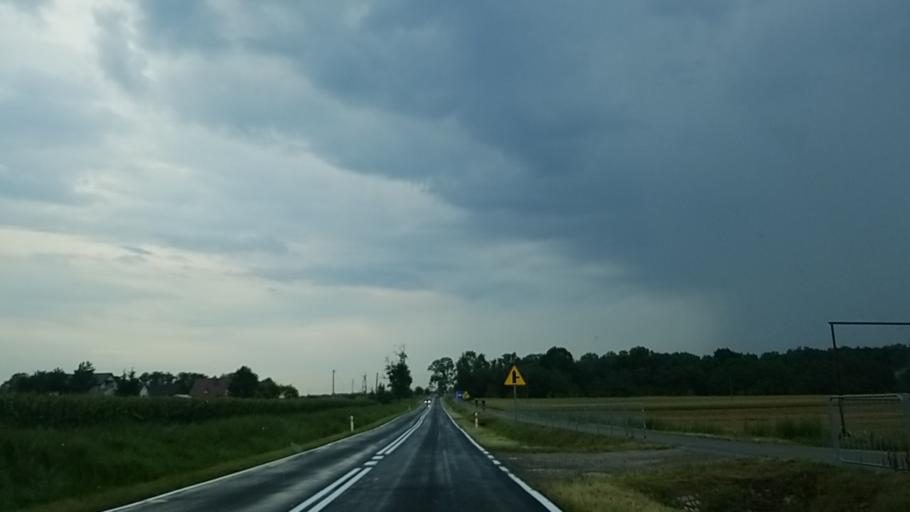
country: PL
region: Lublin Voivodeship
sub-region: Powiat wlodawski
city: Wlodawa
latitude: 51.6042
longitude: 23.5319
